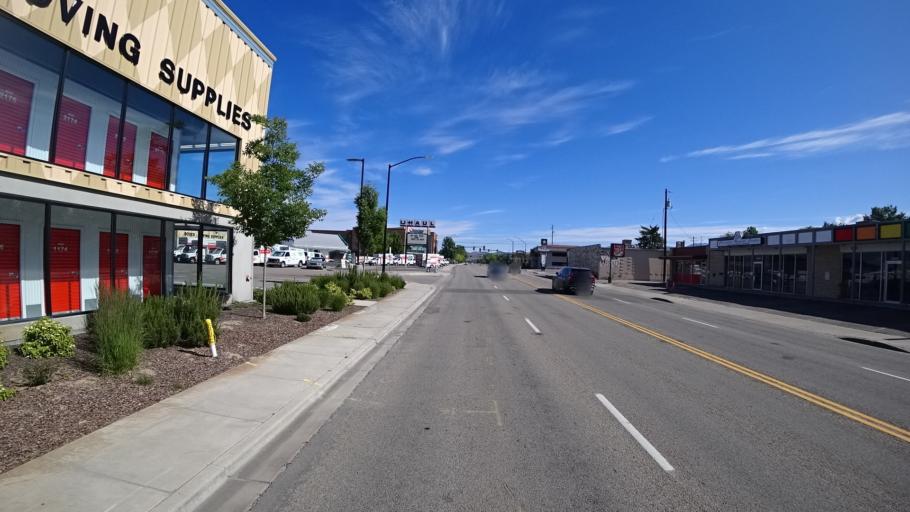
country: US
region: Idaho
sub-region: Ada County
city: Garden City
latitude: 43.6140
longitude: -116.2436
